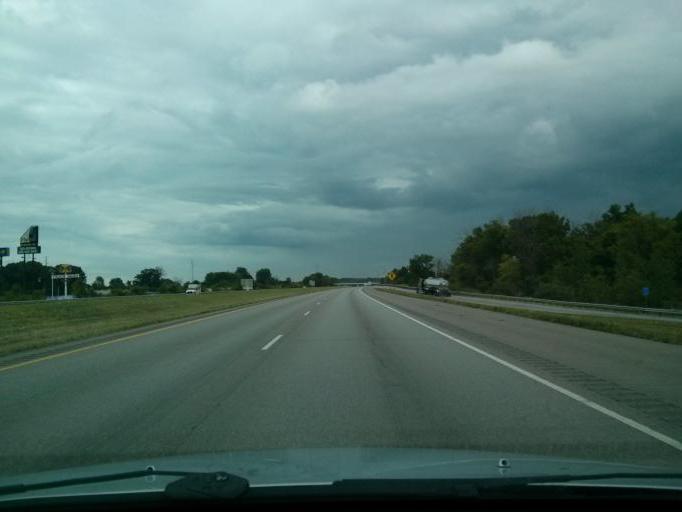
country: US
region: Ohio
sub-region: Trumbull County
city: Hubbard
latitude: 41.1763
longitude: -80.5654
